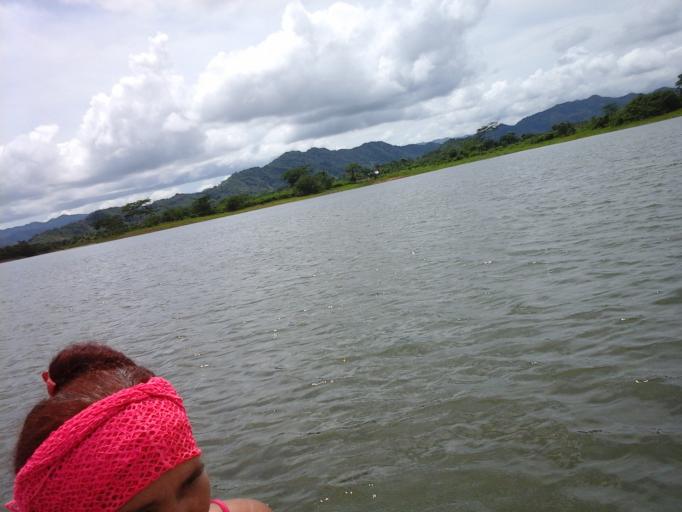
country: CO
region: Bolivar
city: San Cristobal
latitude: 9.8724
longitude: -75.2962
